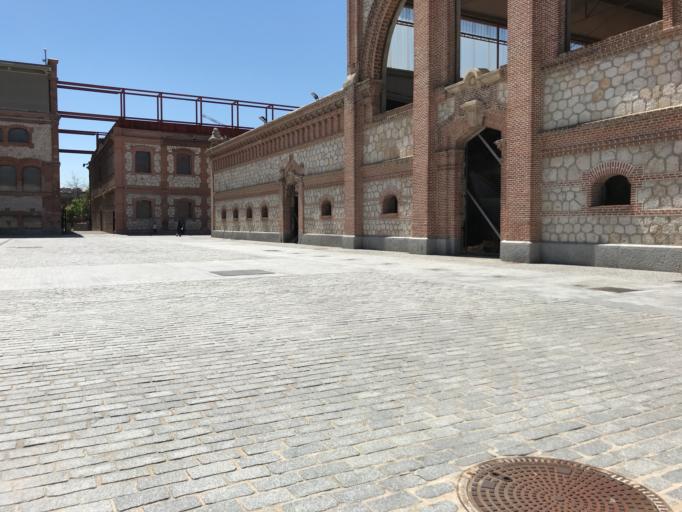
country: ES
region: Madrid
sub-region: Provincia de Madrid
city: Usera
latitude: 40.3912
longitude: -3.6979
